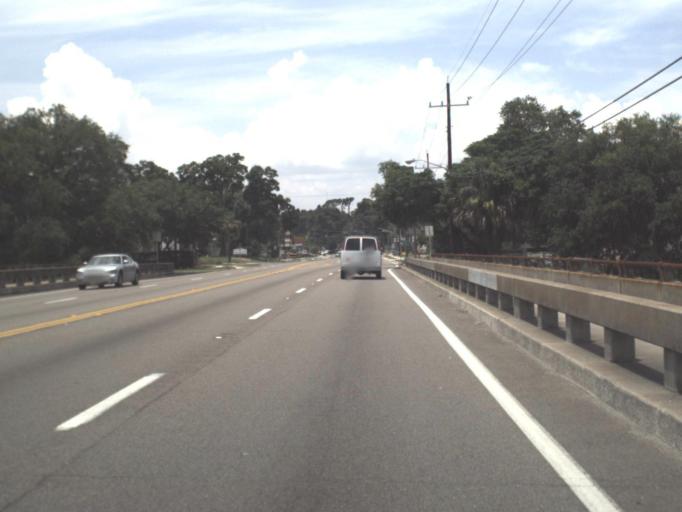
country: US
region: Florida
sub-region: Duval County
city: Jacksonville
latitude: 30.3130
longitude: -81.5952
